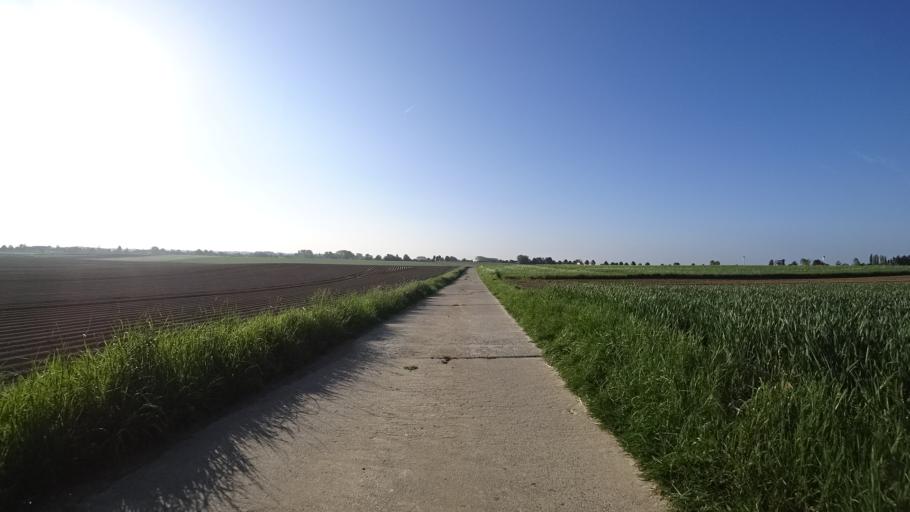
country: BE
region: Wallonia
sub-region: Province du Brabant Wallon
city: Walhain-Saint-Paul
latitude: 50.6217
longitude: 4.7078
